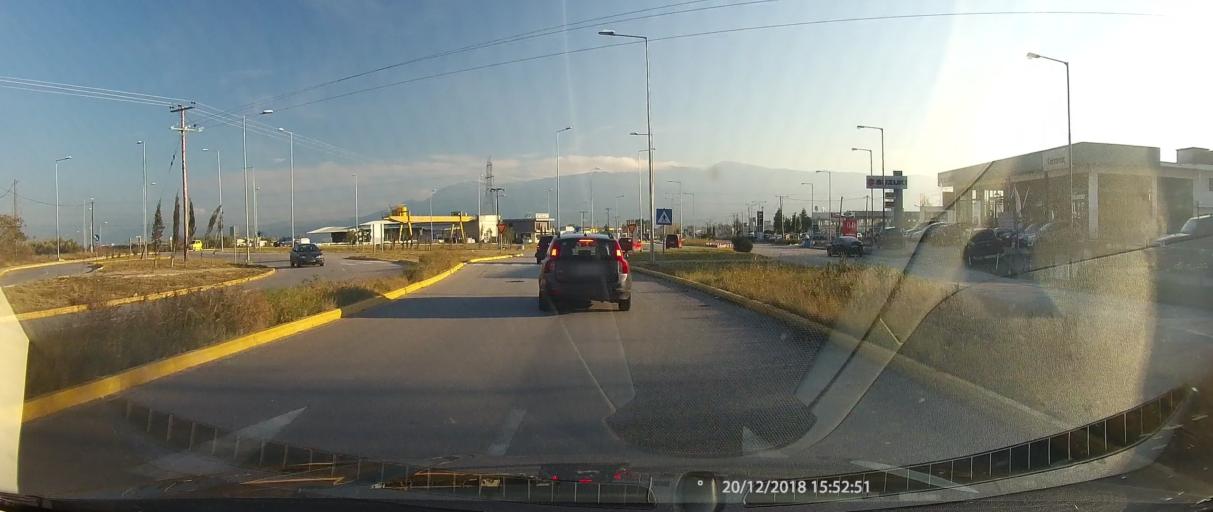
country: GR
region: Central Greece
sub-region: Nomos Fthiotidos
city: Rodhitsa
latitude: 38.8774
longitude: 22.4540
